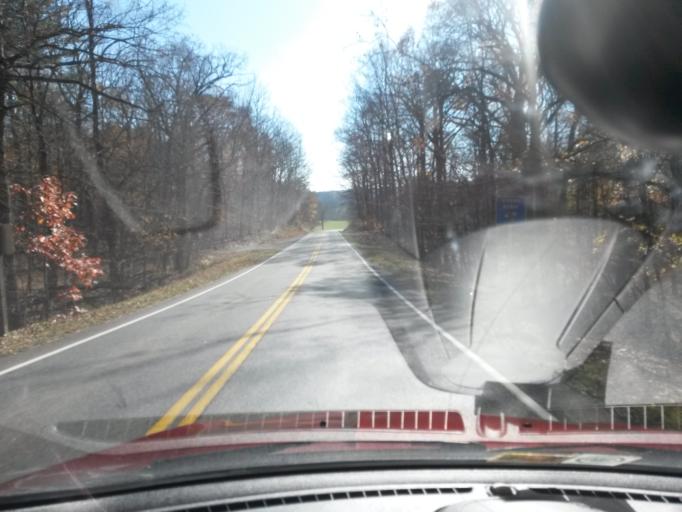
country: US
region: Virginia
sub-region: City of Bedford
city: Bedford
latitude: 37.4056
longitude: -79.5571
